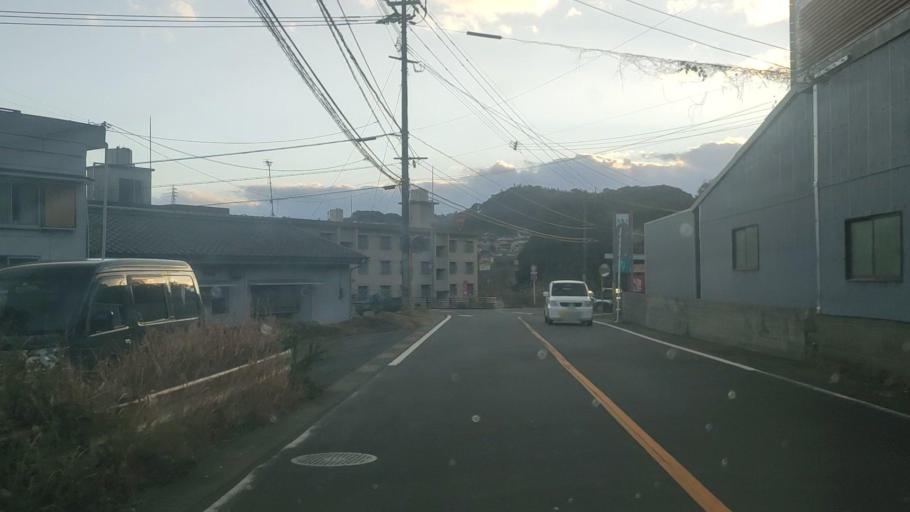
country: JP
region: Kagoshima
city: Kagoshima-shi
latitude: 31.6234
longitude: 130.5425
